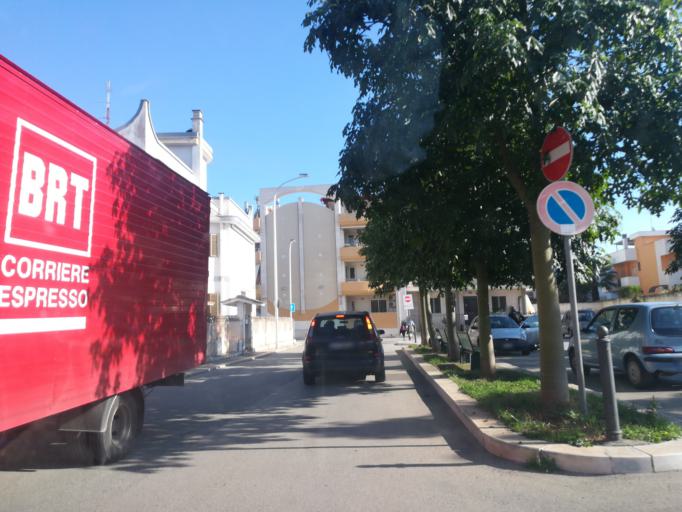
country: IT
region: Apulia
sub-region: Provincia di Bari
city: Modugno
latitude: 41.0779
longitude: 16.7778
